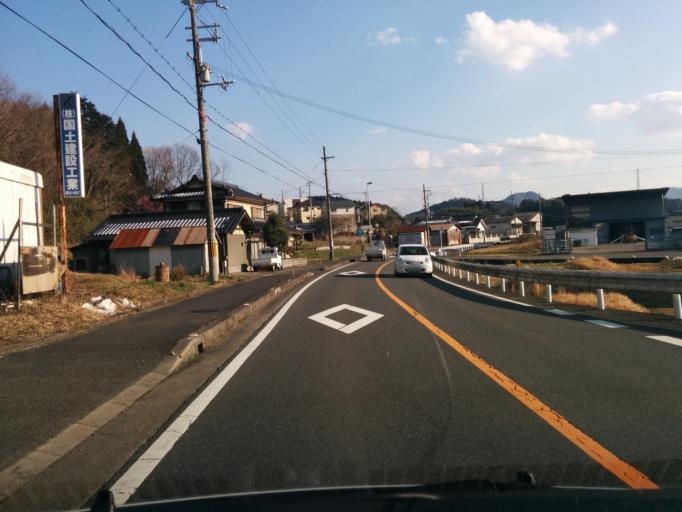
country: JP
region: Kyoto
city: Ayabe
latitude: 35.3337
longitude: 135.2151
